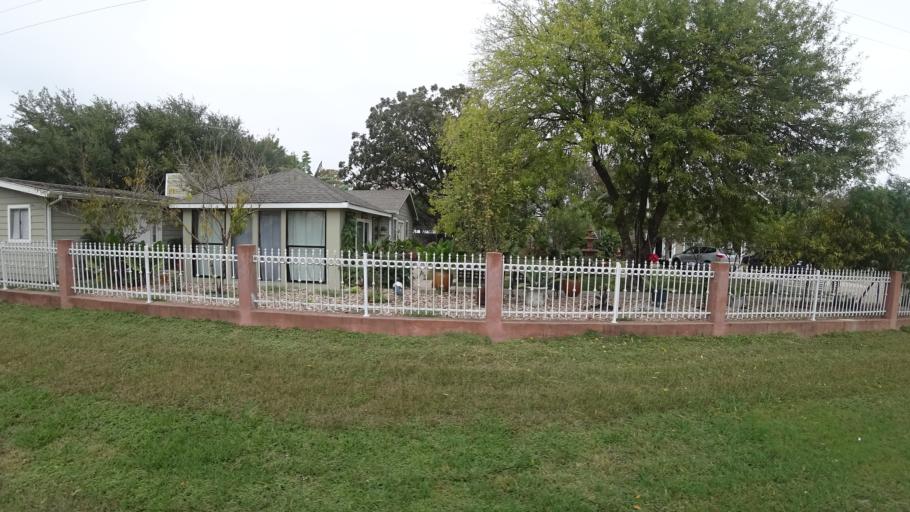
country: US
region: Texas
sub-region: Travis County
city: Pflugerville
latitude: 30.3733
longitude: -97.6222
